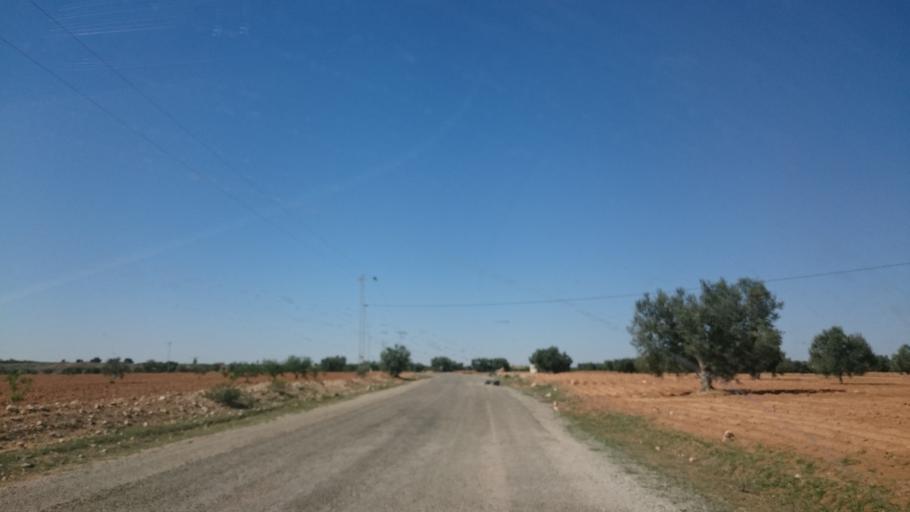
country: TN
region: Safaqis
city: Bi'r `Ali Bin Khalifah
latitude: 34.8654
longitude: 10.3505
